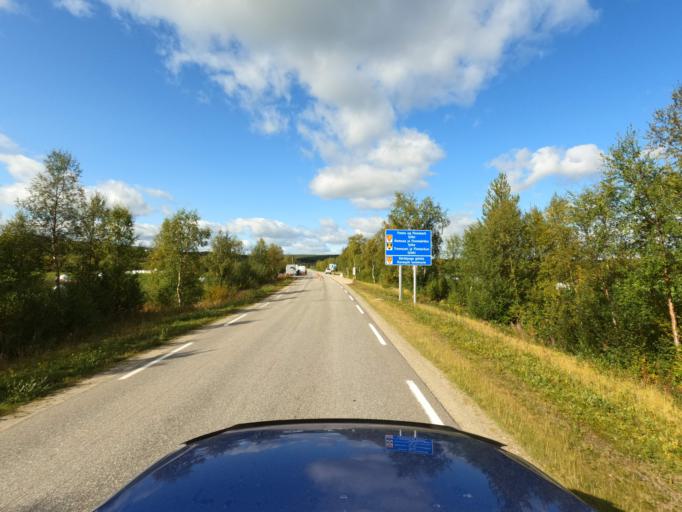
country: NO
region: Finnmark Fylke
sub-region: Karasjok
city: Karasjohka
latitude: 69.3994
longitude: 25.8346
